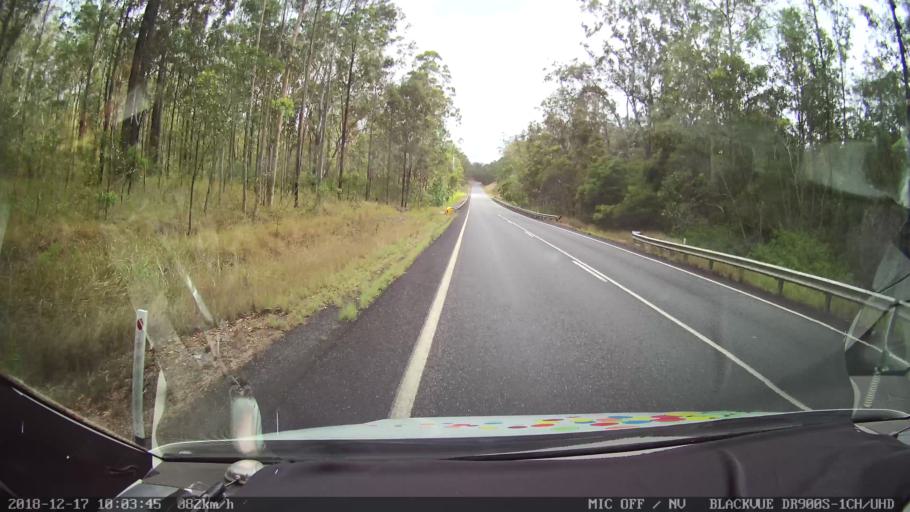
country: AU
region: New South Wales
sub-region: Tenterfield Municipality
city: Carrolls Creek
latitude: -28.8965
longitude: 152.4682
